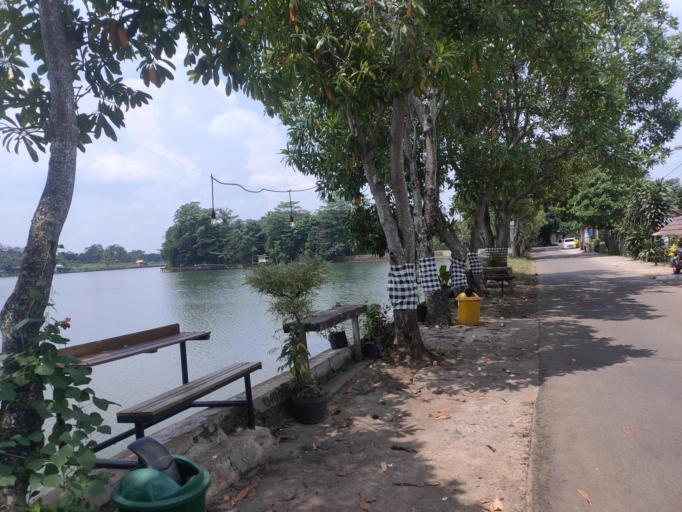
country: ID
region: West Java
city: Parung
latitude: -6.4705
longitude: 106.7138
